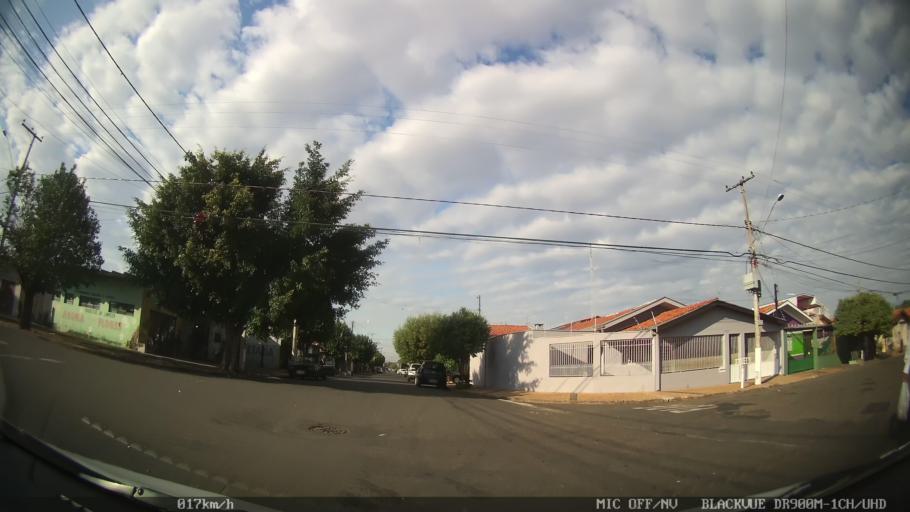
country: BR
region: Sao Paulo
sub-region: Americana
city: Americana
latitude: -22.7271
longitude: -47.3626
